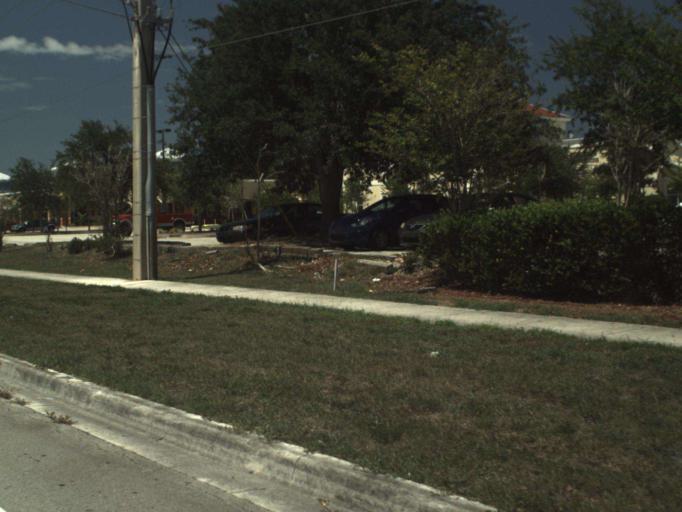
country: US
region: Florida
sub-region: Saint Lucie County
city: River Park
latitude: 27.3018
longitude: -80.3061
